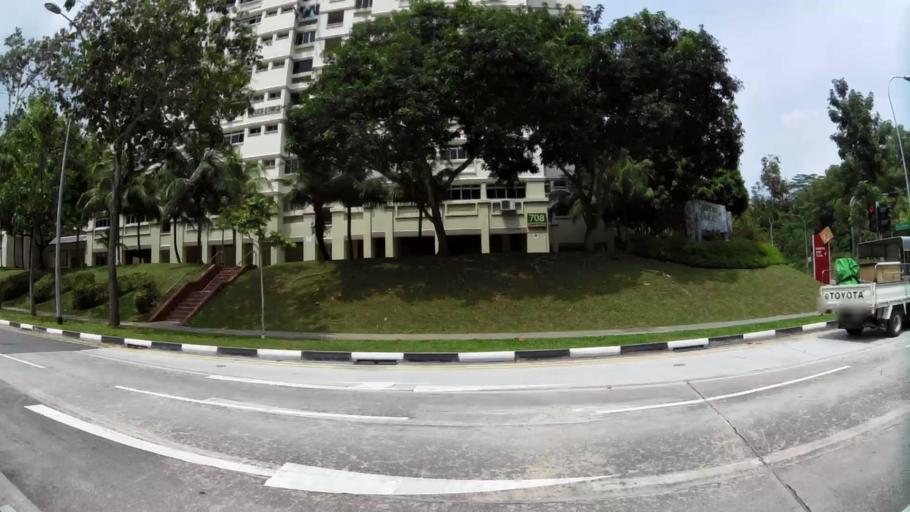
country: MY
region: Johor
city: Kampung Pasir Gudang Baru
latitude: 1.3812
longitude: 103.9394
